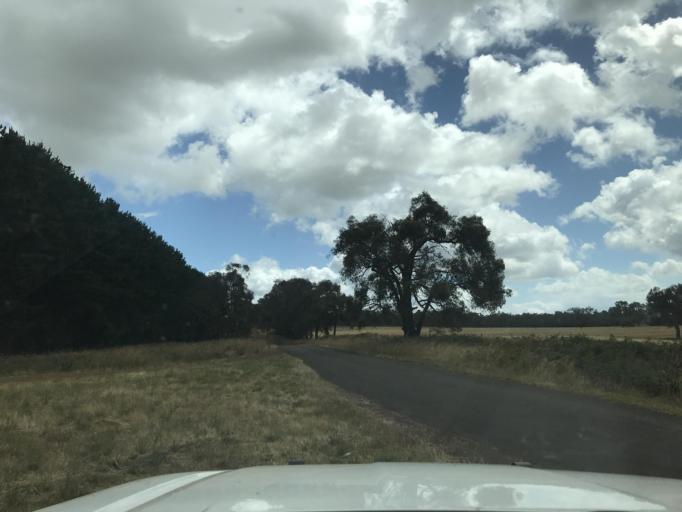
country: AU
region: South Australia
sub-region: Wattle Range
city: Penola
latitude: -37.2114
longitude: 141.4811
